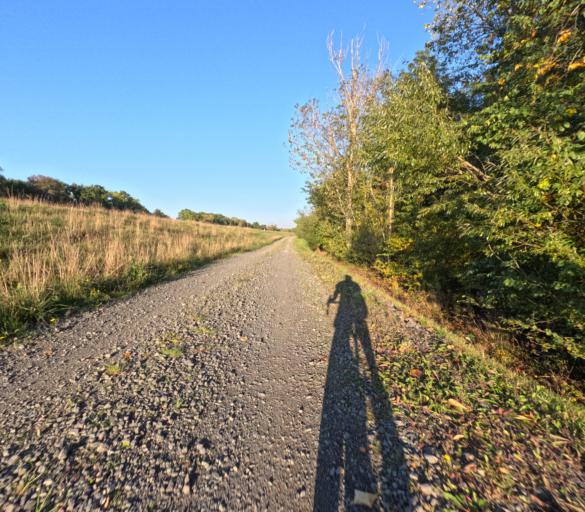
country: DE
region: Saxony
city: Schkeuditz
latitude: 51.3796
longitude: 12.2530
